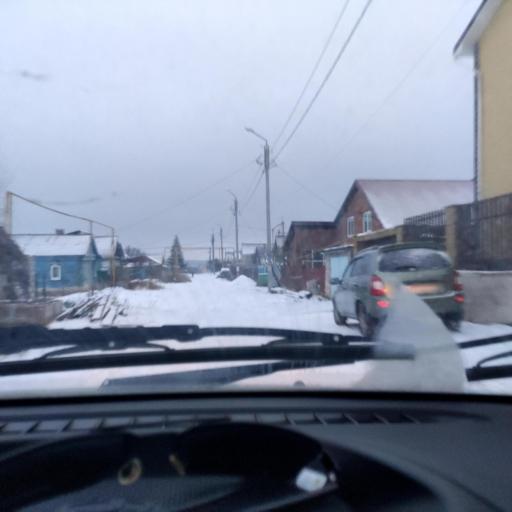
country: RU
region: Samara
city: Zhigulevsk
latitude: 53.4868
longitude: 49.5312
